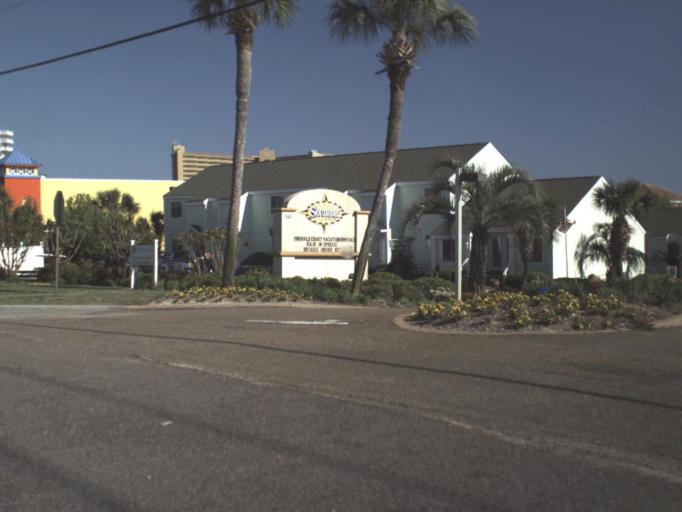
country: US
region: Florida
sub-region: Okaloosa County
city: Destin
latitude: 30.3884
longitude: -86.4786
